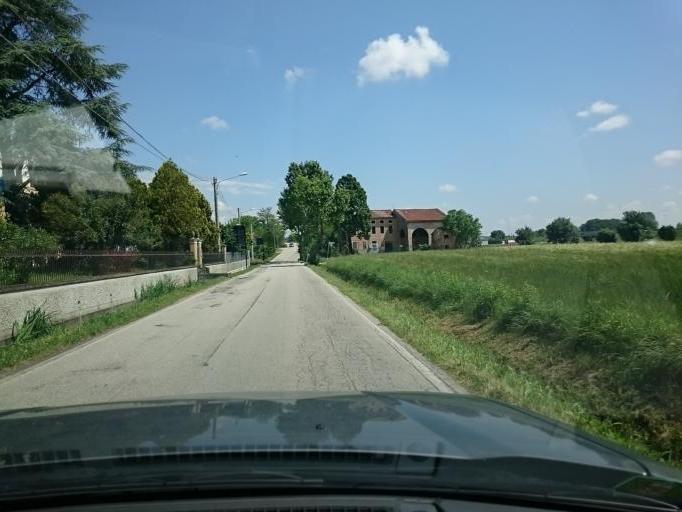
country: IT
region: Veneto
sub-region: Provincia di Vicenza
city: Torri di Quartesolo
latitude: 45.5102
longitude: 11.5961
